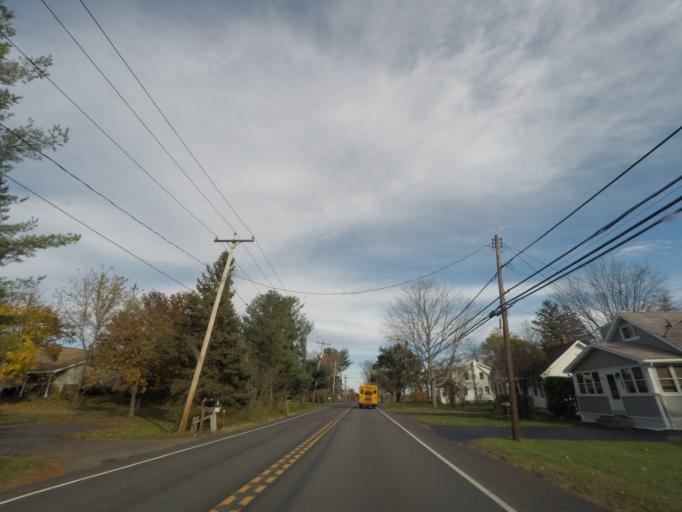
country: US
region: New York
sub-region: Albany County
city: Delmar
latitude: 42.6011
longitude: -73.8874
